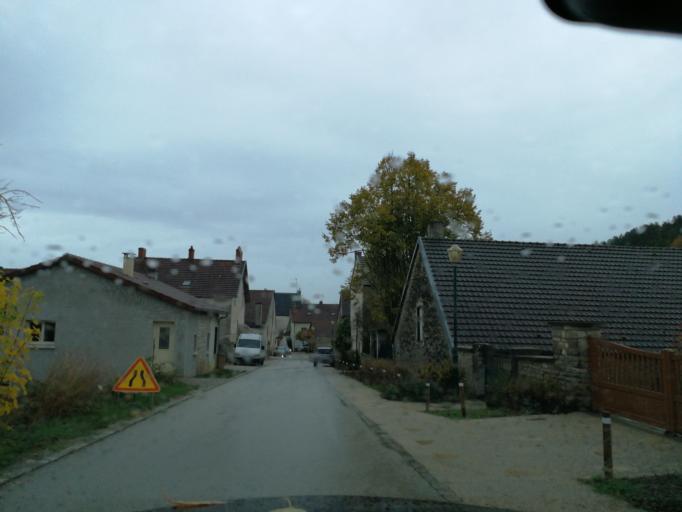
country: FR
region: Bourgogne
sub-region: Departement de la Cote-d'Or
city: Fleurey-sur-Ouche
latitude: 47.3236
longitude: 4.7917
